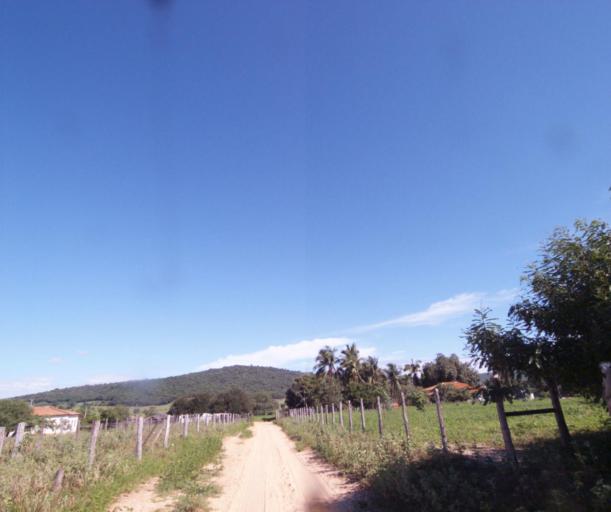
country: BR
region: Bahia
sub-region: Sao Felix Do Coribe
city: Santa Maria da Vitoria
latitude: -13.6173
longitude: -44.4139
